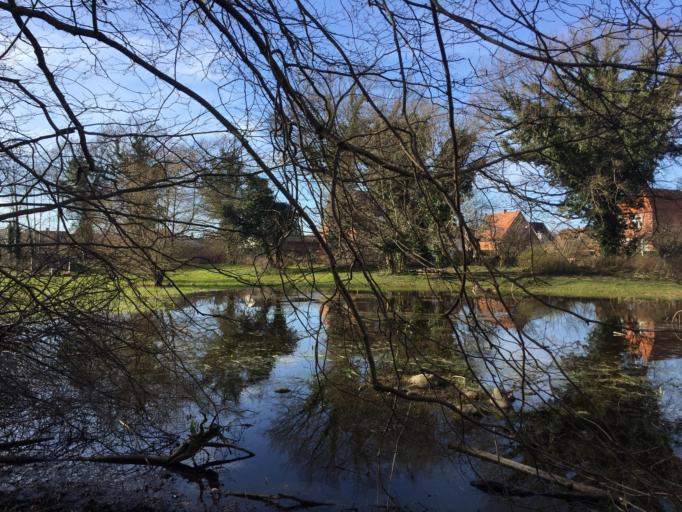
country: DK
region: South Denmark
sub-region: Odense Kommune
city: Odense
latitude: 55.4057
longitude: 10.3486
